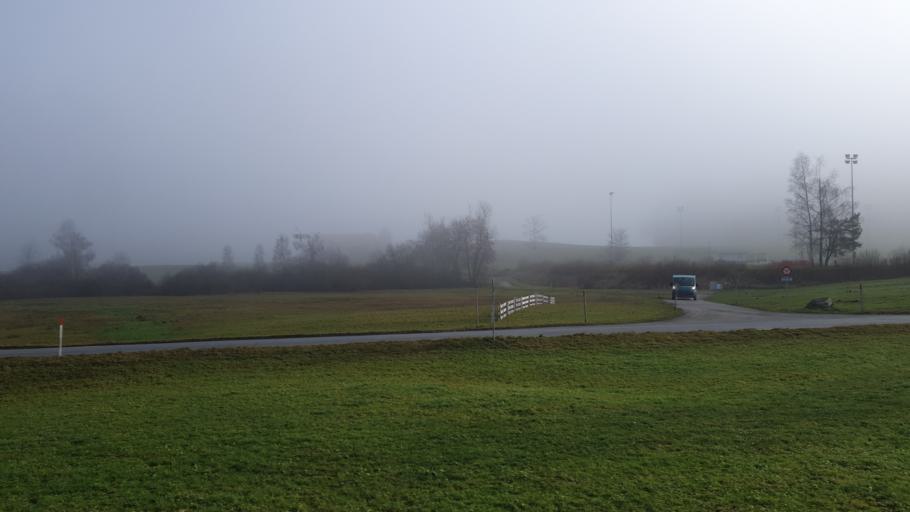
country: CH
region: Fribourg
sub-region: Veveyse District
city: Chatel-Saint-Denis
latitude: 46.5395
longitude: 6.8971
